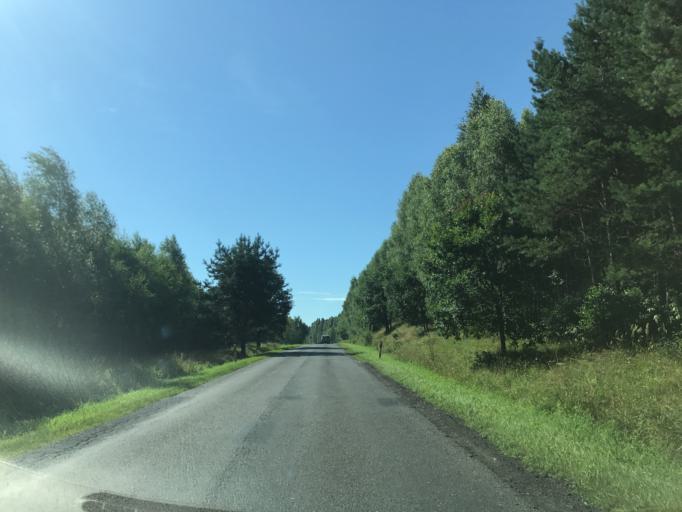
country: PL
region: Pomeranian Voivodeship
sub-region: Powiat bytowski
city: Czarna Dabrowka
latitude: 54.3736
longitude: 17.5004
